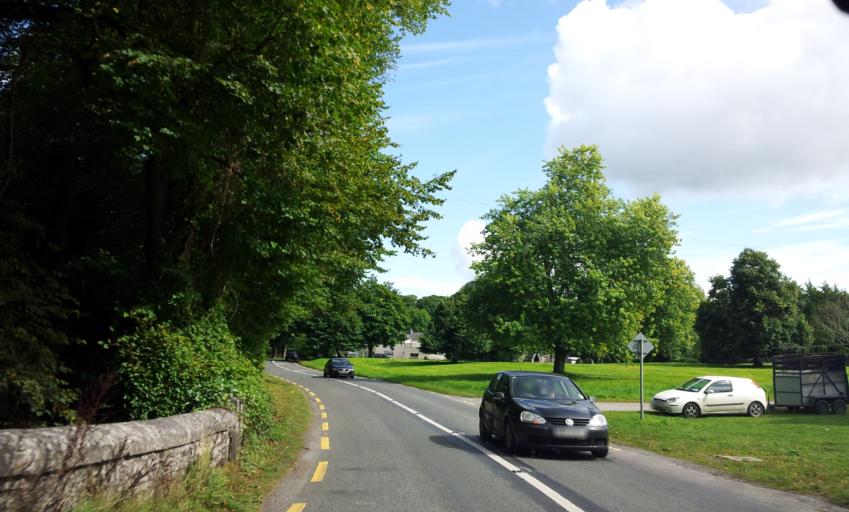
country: IE
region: Munster
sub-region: Ciarrai
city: Cill Airne
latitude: 52.0257
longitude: -9.4895
